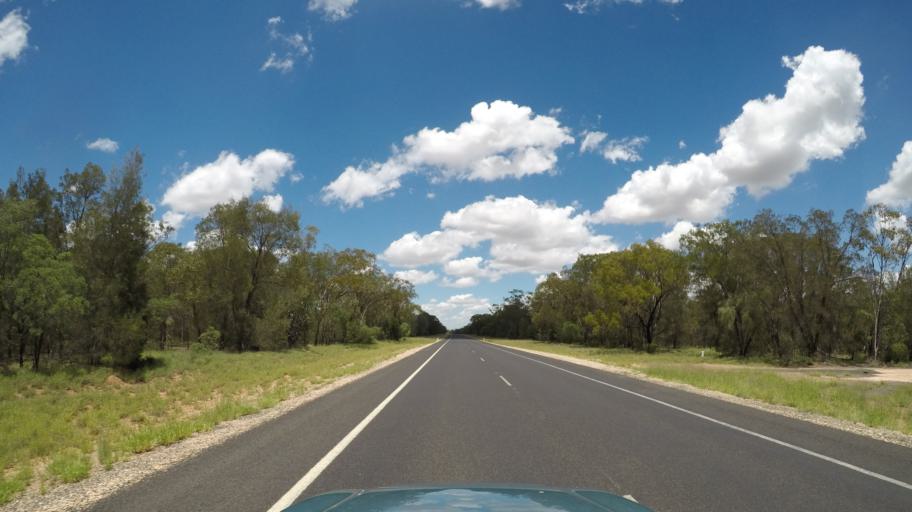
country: AU
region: Queensland
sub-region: Goondiwindi
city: Goondiwindi
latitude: -28.0589
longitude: 150.7684
